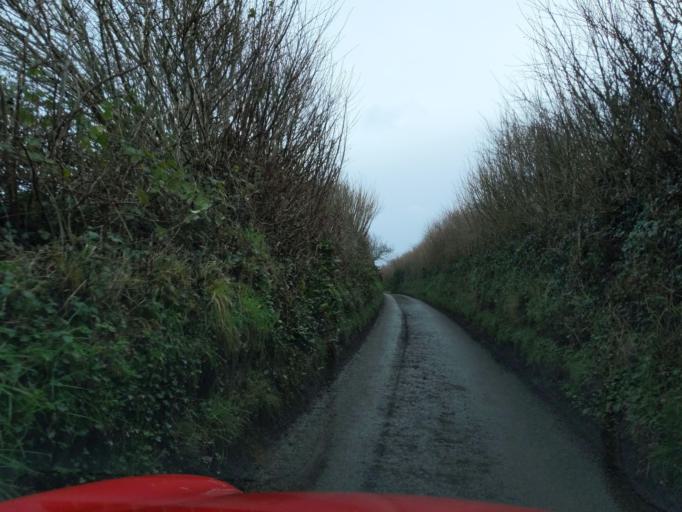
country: GB
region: England
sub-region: Cornwall
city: Duloe
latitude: 50.3536
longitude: -4.5149
